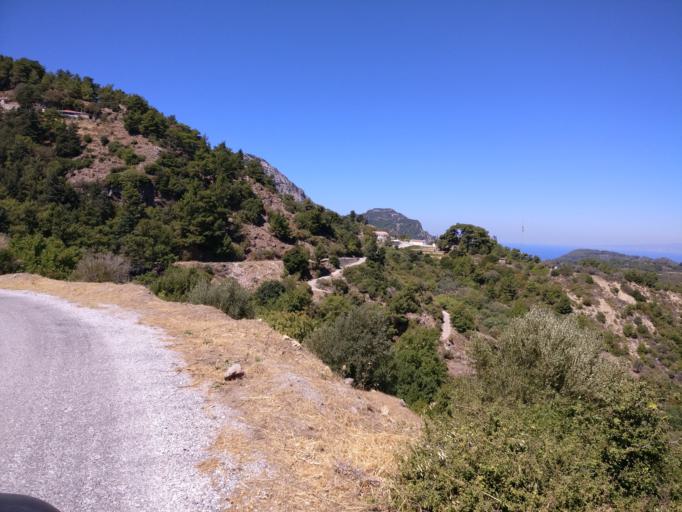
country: GR
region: North Aegean
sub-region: Nomos Samou
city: Marathokampos
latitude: 37.7496
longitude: 26.6928
